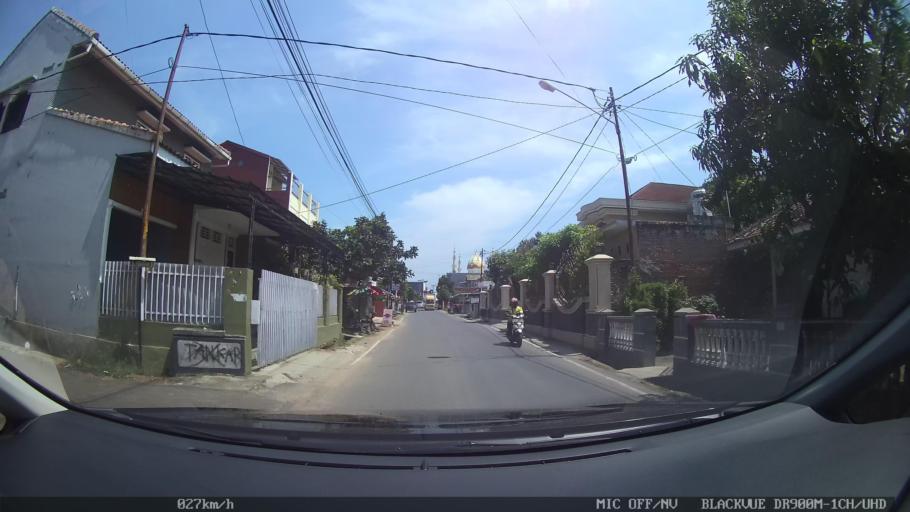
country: ID
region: Lampung
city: Kedaton
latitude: -5.3867
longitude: 105.2765
